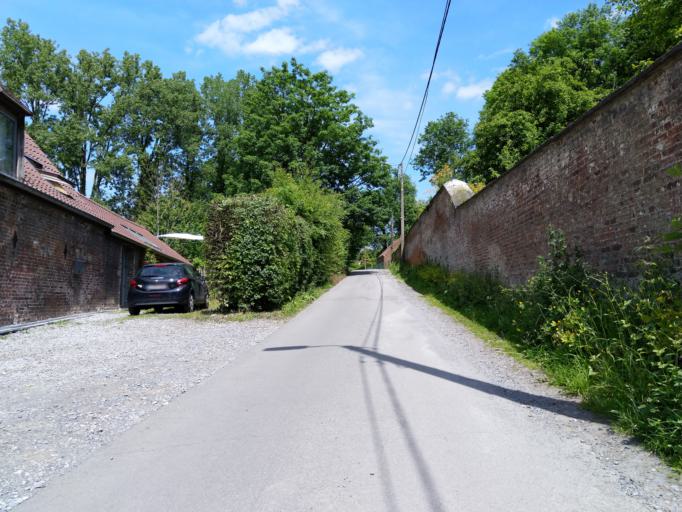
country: BE
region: Wallonia
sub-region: Province du Hainaut
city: Mons
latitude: 50.4946
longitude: 4.0204
